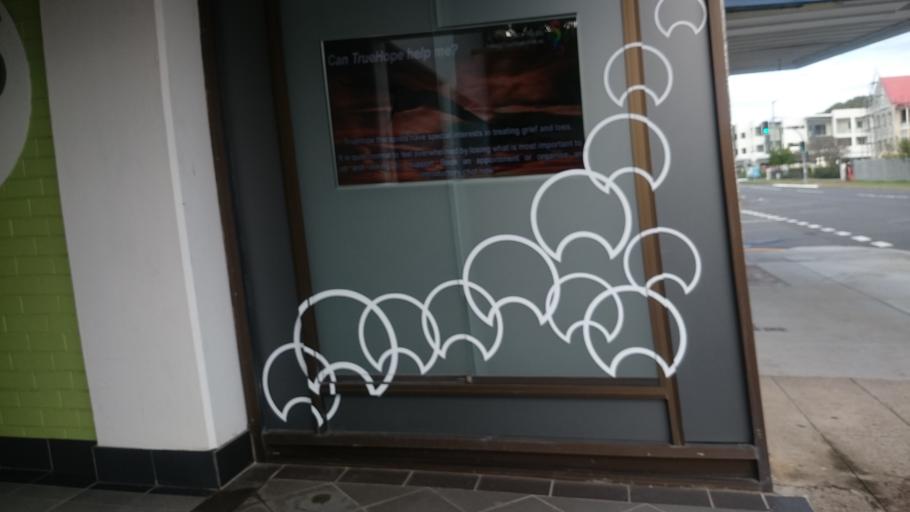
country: AU
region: Queensland
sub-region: Brisbane
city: Wynnum
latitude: -27.4455
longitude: 153.1755
